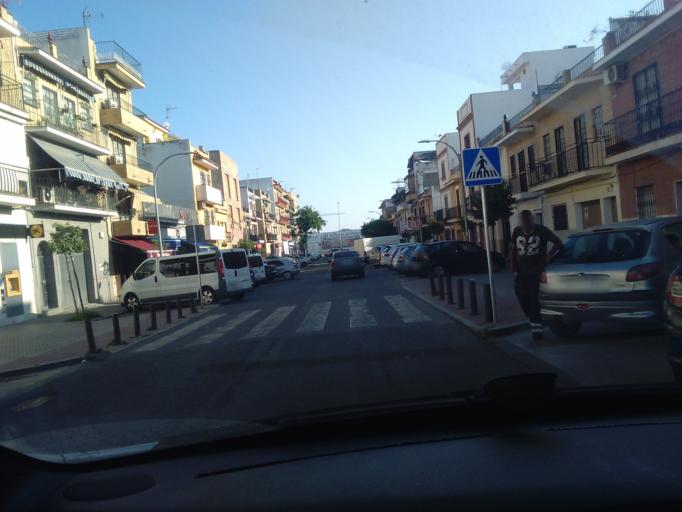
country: ES
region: Andalusia
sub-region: Provincia de Sevilla
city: Sevilla
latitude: 37.3834
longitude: -5.9038
